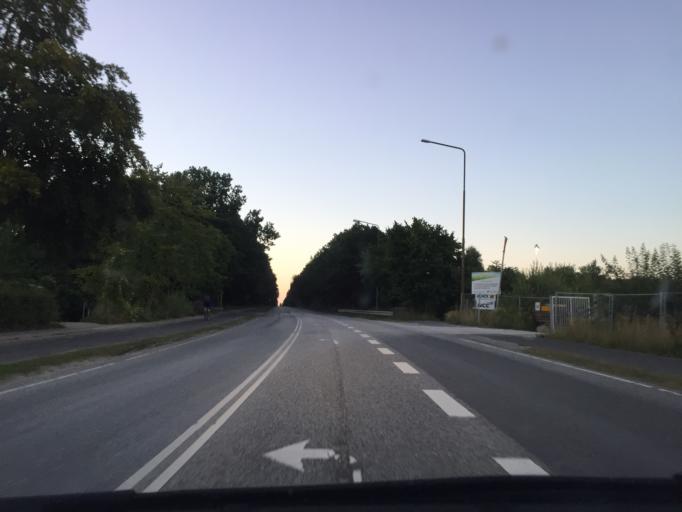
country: DK
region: Capital Region
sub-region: Lyngby-Tarbaek Kommune
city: Kongens Lyngby
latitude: 55.7794
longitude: 12.5242
